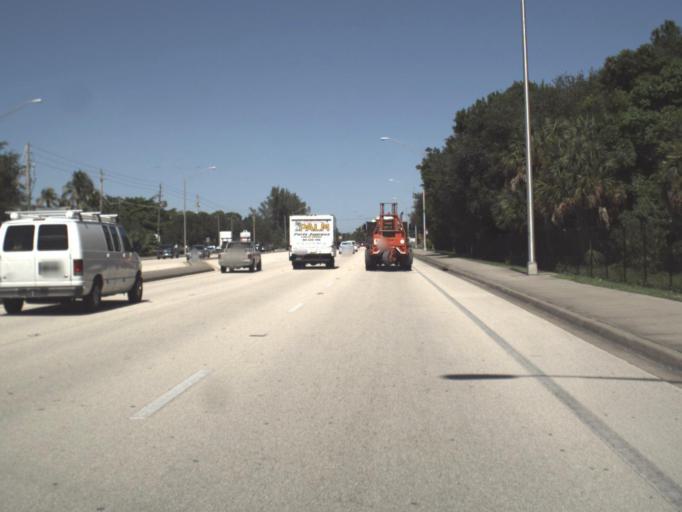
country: US
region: Florida
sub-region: Collier County
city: Naples Park
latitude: 26.2779
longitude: -81.8016
